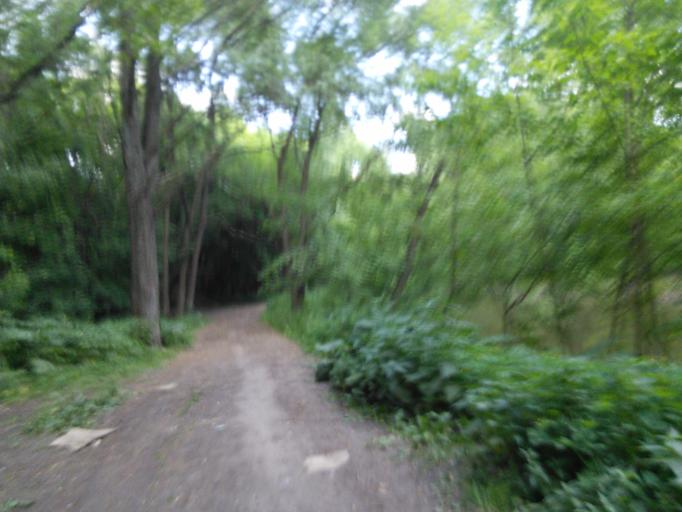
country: RU
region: Moskovskaya
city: Bogorodskoye
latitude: 55.8110
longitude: 37.6968
